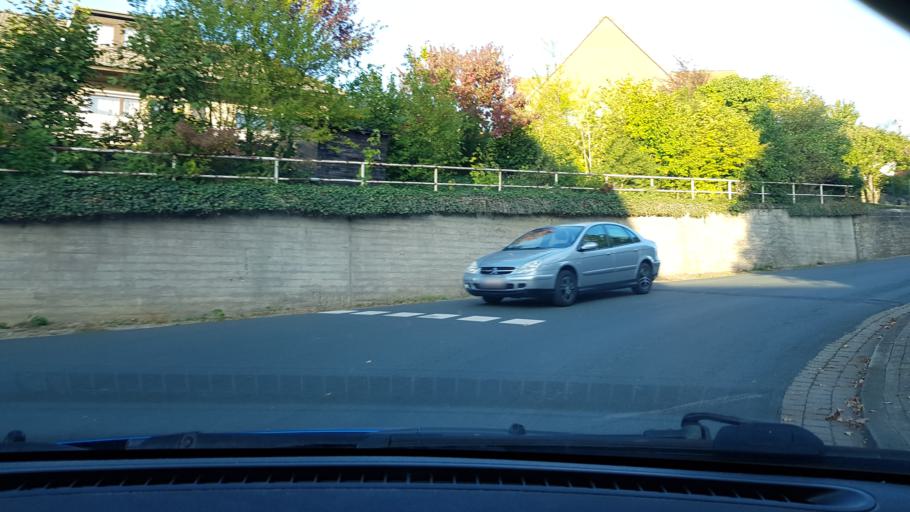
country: DE
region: Lower Saxony
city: Lauenau
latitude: 52.2852
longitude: 9.3813
